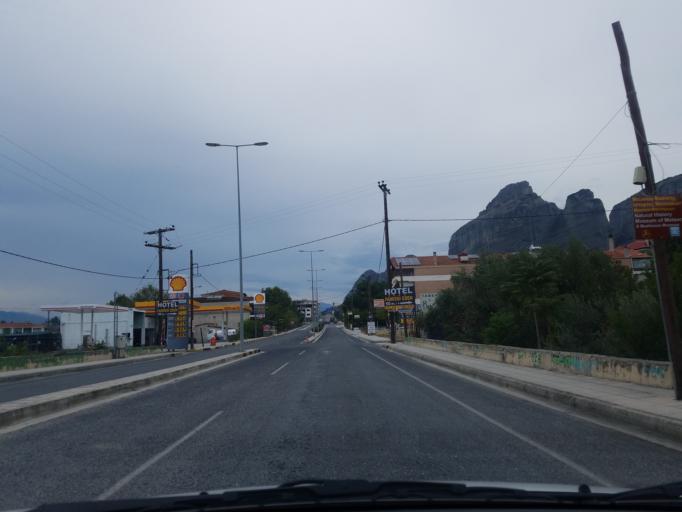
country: GR
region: Thessaly
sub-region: Trikala
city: Kalampaka
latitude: 39.7007
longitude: 21.6359
